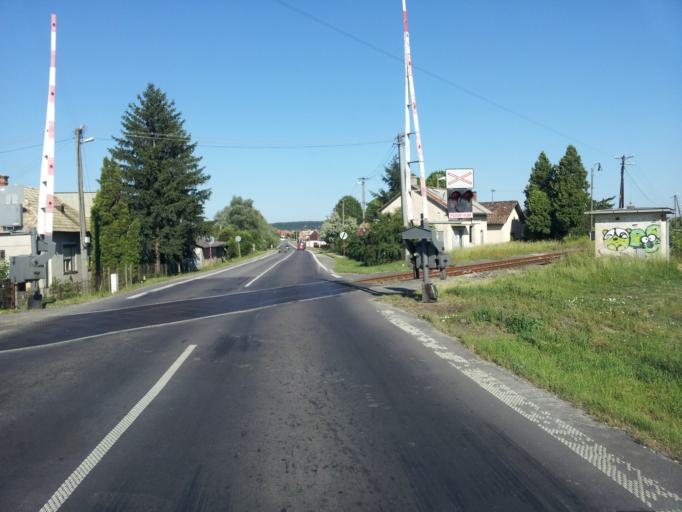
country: SK
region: Nitriansky
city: Sahy
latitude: 48.0870
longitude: 18.9096
